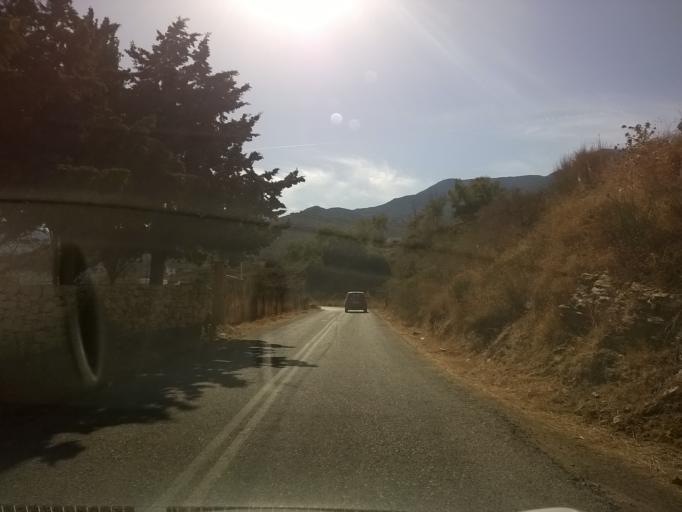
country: GR
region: South Aegean
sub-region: Nomos Kykladon
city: Filotion
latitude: 37.1765
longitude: 25.5492
